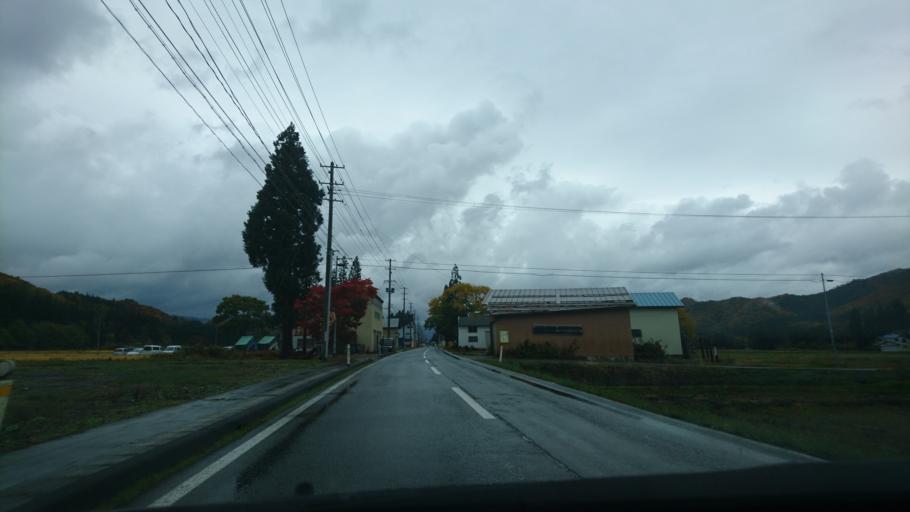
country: JP
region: Akita
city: Yokotemachi
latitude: 39.3655
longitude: 140.7616
